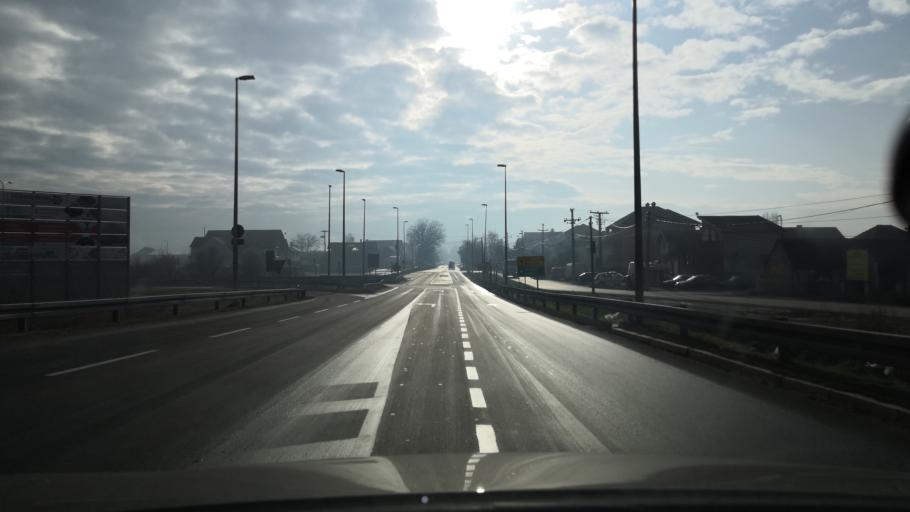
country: RS
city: Dobanovci
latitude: 44.8424
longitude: 20.2126
